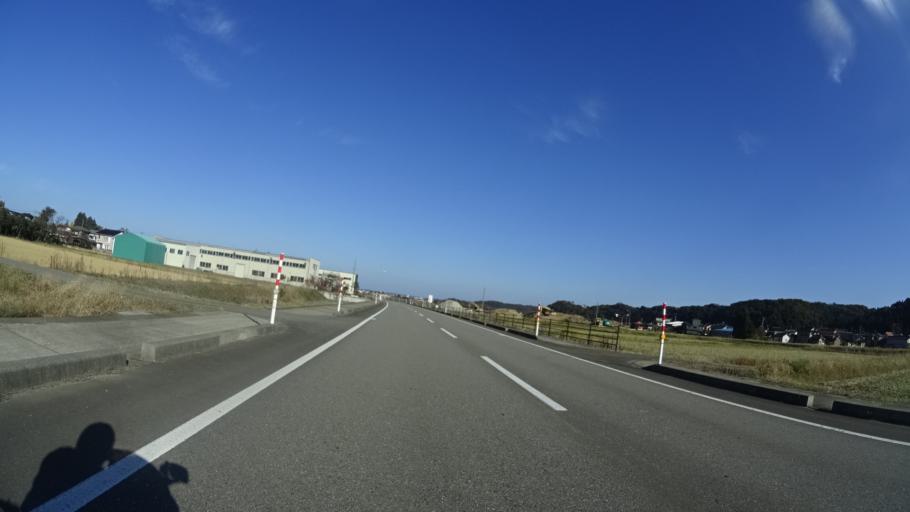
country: JP
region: Ishikawa
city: Komatsu
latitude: 36.2893
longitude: 136.3897
